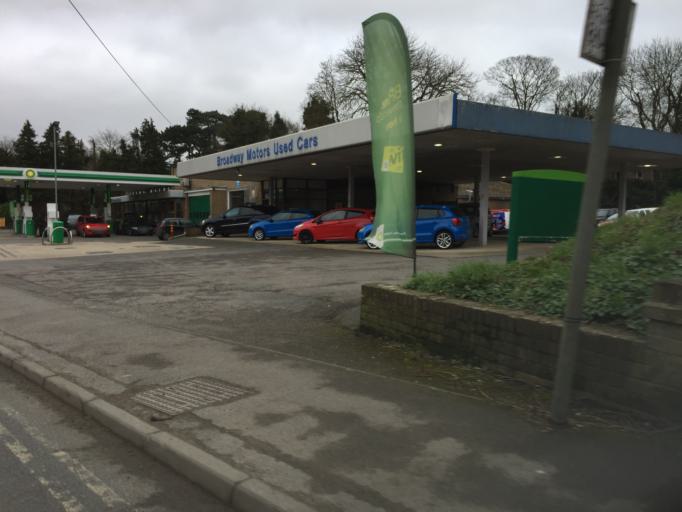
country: GB
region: England
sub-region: Oxfordshire
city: Wantage
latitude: 51.5885
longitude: -1.4226
